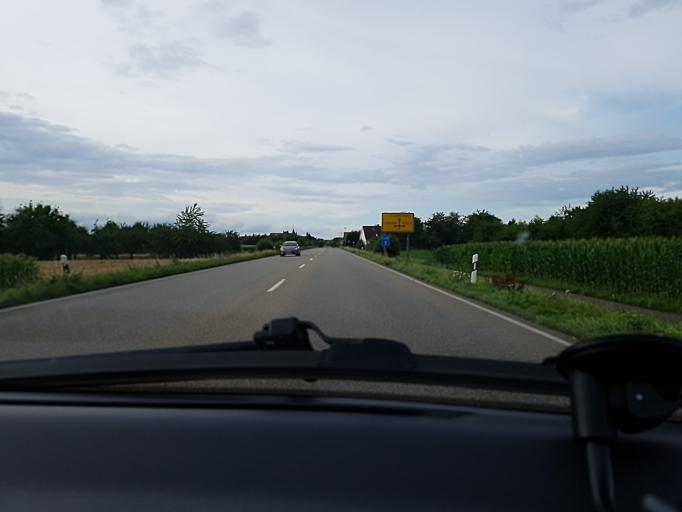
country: DE
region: Baden-Wuerttemberg
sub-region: Freiburg Region
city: Appenweier
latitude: 48.5119
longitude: 7.9623
